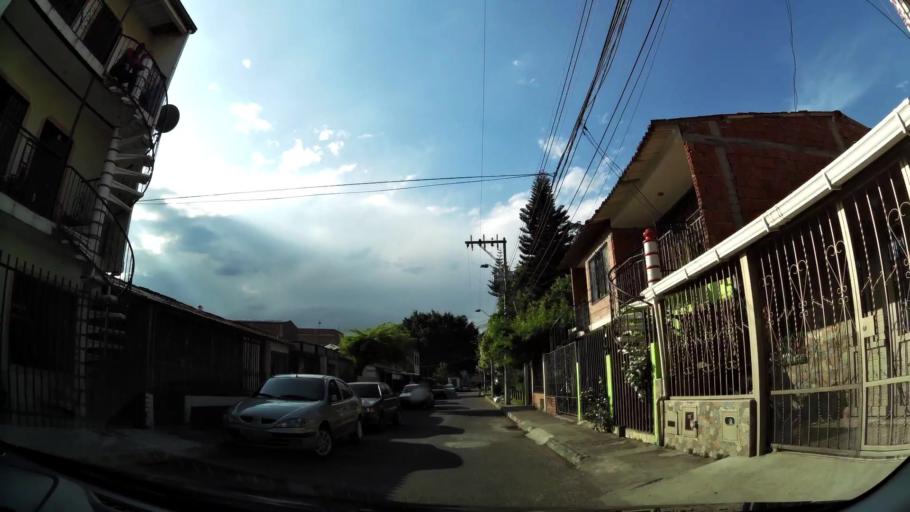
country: CO
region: Valle del Cauca
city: Cali
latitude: 3.4005
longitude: -76.5077
